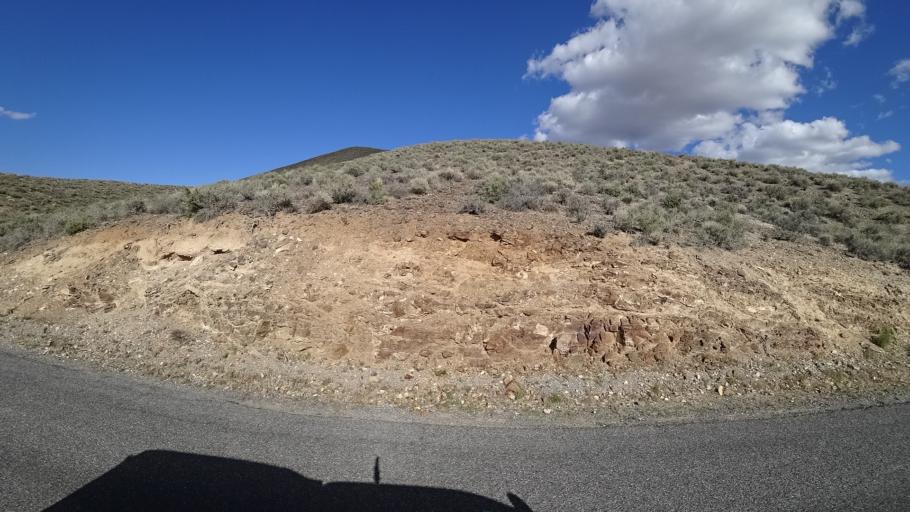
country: US
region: California
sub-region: San Bernardino County
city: Searles Valley
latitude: 36.3225
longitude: -117.1515
